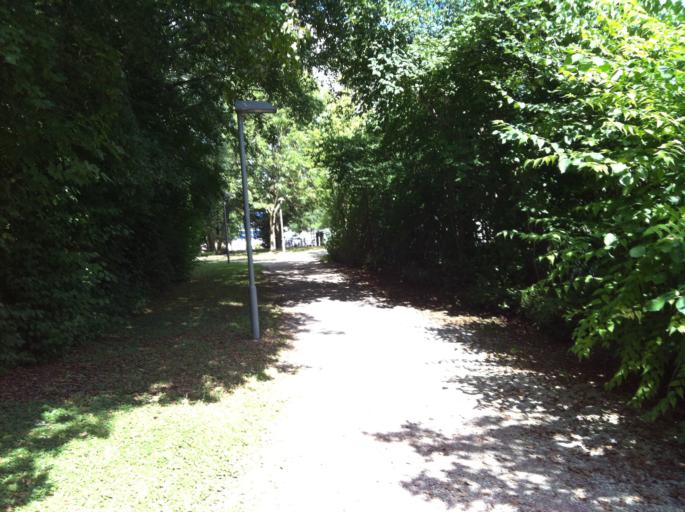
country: DE
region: Bavaria
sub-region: Upper Bavaria
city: Garching bei Munchen
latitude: 48.2660
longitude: 11.6673
